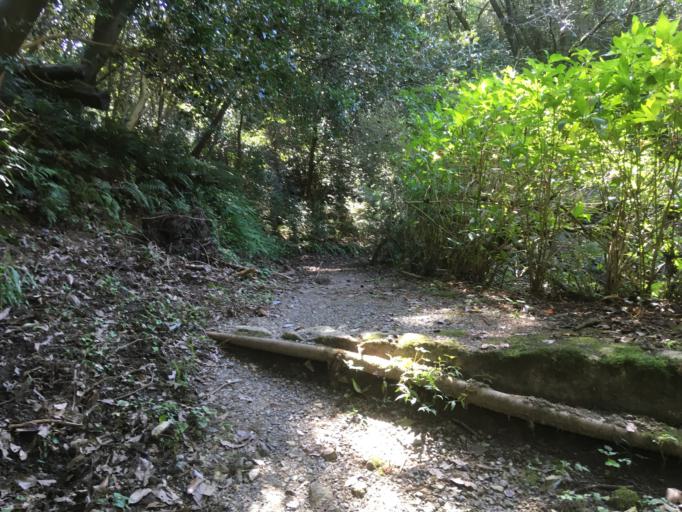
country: JP
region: Nara
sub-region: Ikoma-shi
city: Ikoma
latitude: 34.7265
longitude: 135.6763
